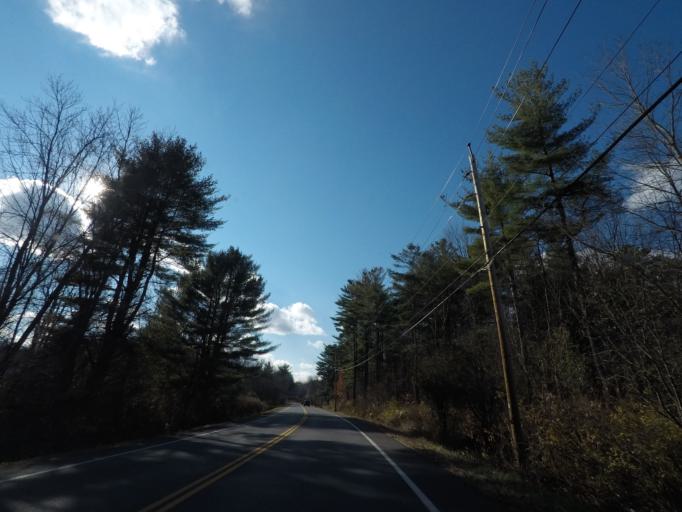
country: US
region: New York
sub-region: Saratoga County
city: Country Knolls
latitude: 42.8904
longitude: -73.7878
